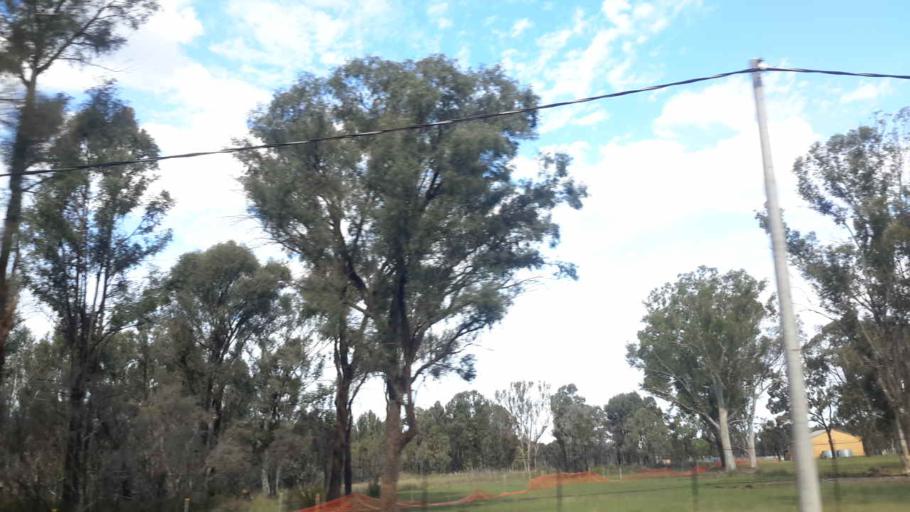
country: AU
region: New South Wales
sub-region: Penrith Municipality
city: Werrington Downs
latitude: -33.6979
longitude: 150.7273
